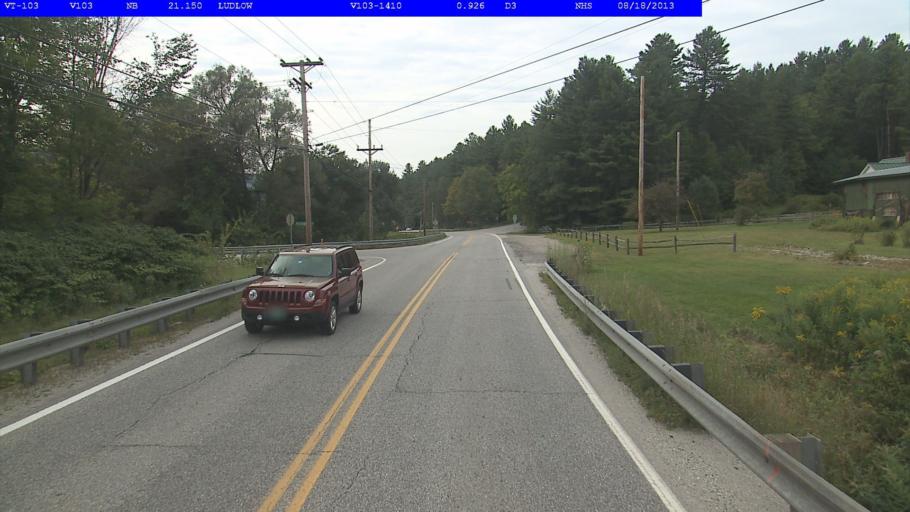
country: US
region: Vermont
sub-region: Windsor County
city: Chester
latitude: 43.3928
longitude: -72.6783
